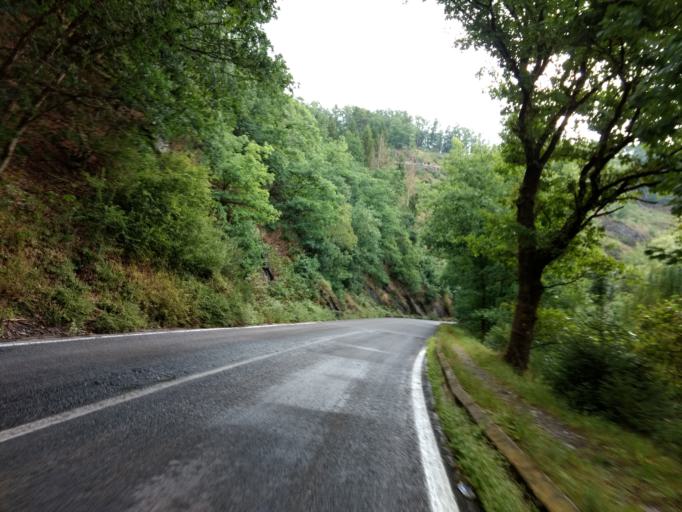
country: BE
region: Wallonia
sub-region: Province du Luxembourg
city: Houffalize
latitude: 50.1341
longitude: 5.7653
